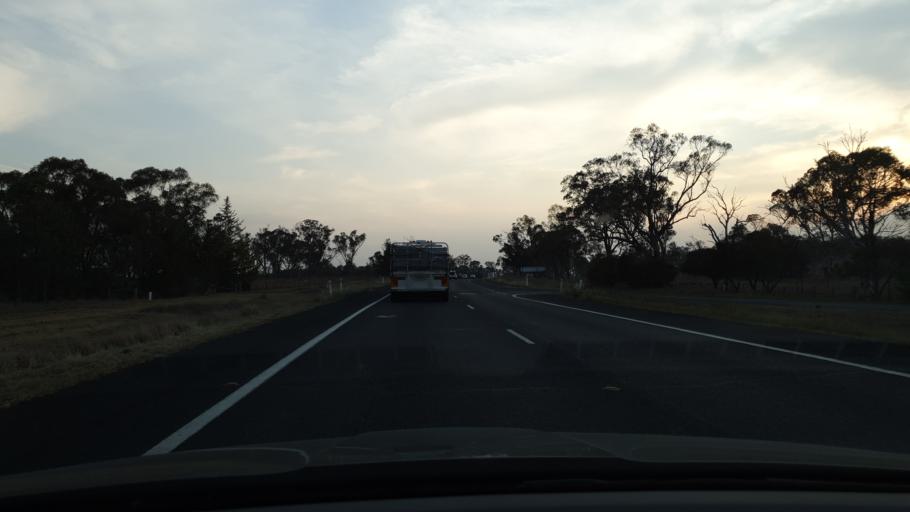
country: AU
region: New South Wales
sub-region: Glen Innes Severn
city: Glen Innes
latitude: -29.6640
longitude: 151.7772
